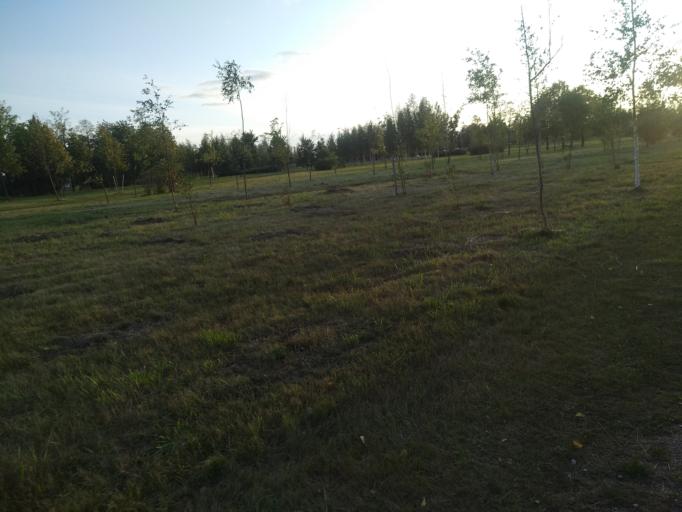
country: RU
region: St.-Petersburg
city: Pushkin
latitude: 59.7456
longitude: 30.3987
